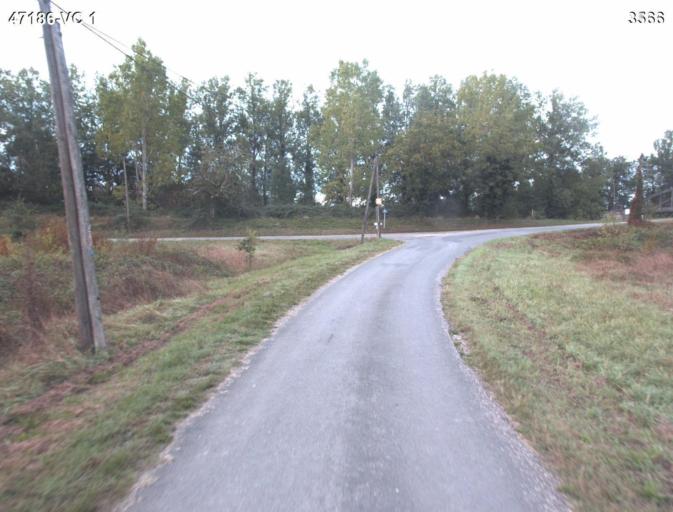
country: FR
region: Aquitaine
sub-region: Departement du Lot-et-Garonne
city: Port-Sainte-Marie
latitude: 44.2180
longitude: 0.4440
